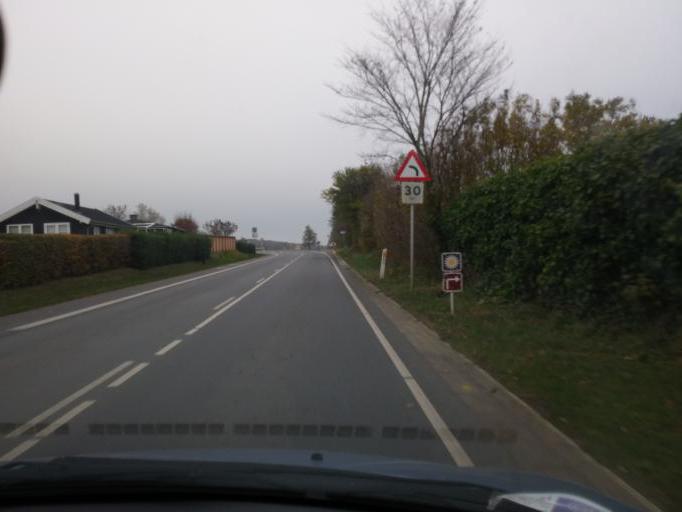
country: DK
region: South Denmark
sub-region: Kerteminde Kommune
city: Kerteminde
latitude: 55.4661
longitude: 10.6765
